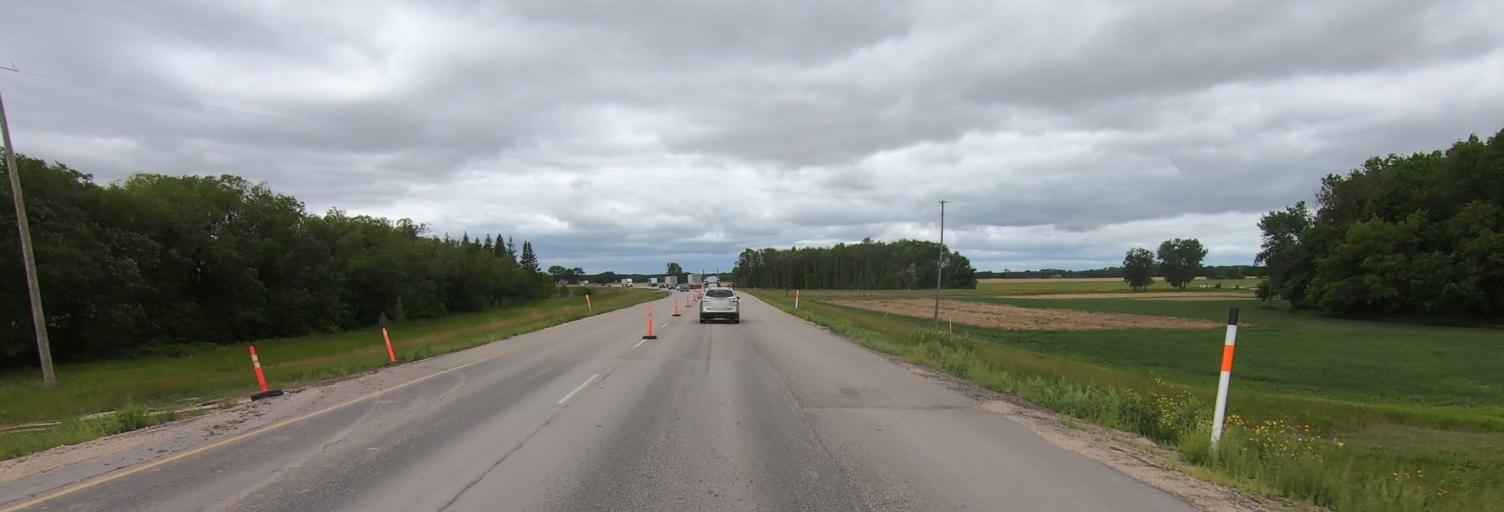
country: CA
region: Manitoba
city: Portage la Prairie
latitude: 49.9715
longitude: -98.0992
